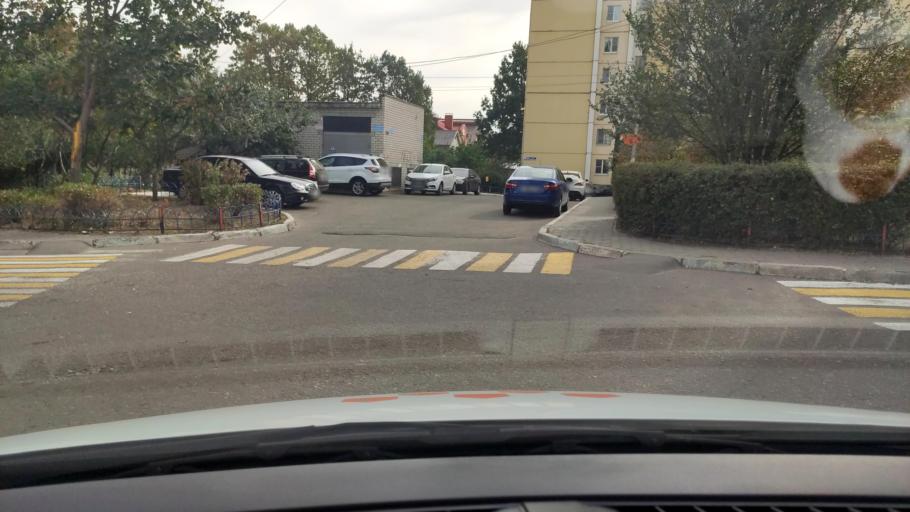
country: RU
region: Voronezj
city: Voronezh
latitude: 51.7121
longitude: 39.1921
